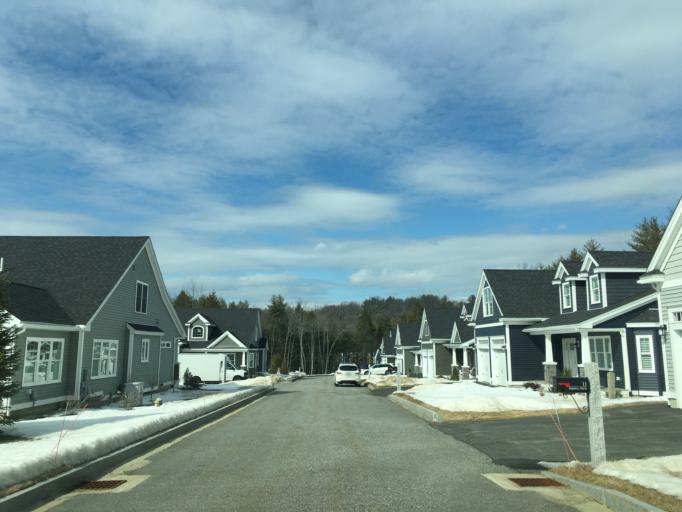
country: US
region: New Hampshire
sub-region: Rockingham County
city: Exeter
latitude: 42.9820
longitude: -70.8910
